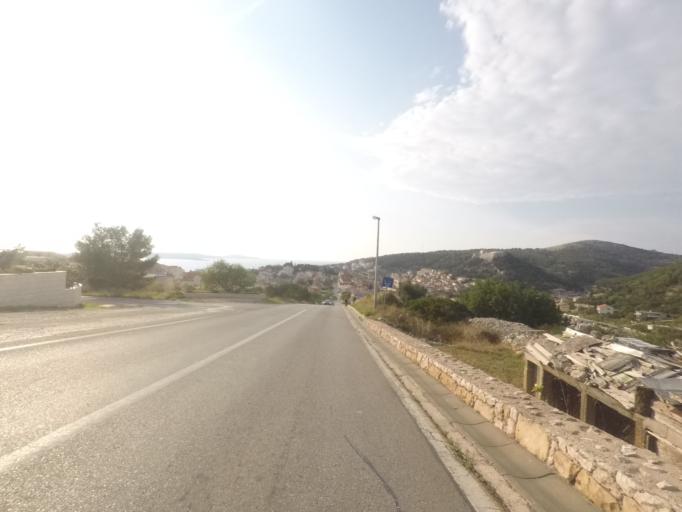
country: HR
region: Splitsko-Dalmatinska
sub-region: Grad Hvar
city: Hvar
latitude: 43.1697
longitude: 16.4500
